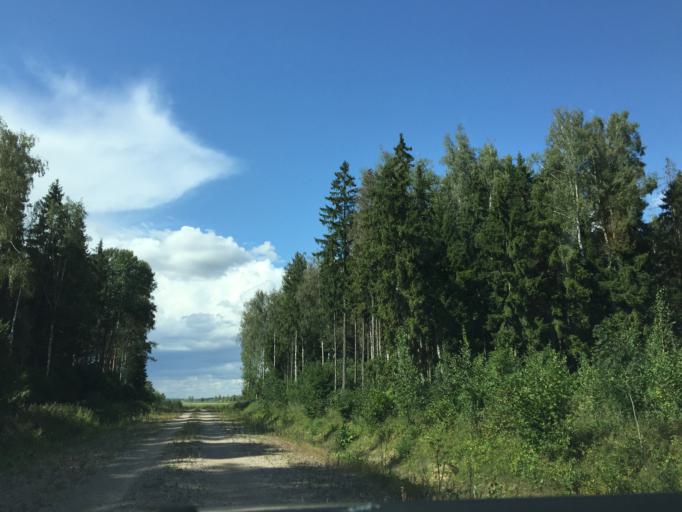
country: LT
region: Siauliu apskritis
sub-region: Joniskis
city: Joniskis
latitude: 56.3566
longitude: 23.5856
